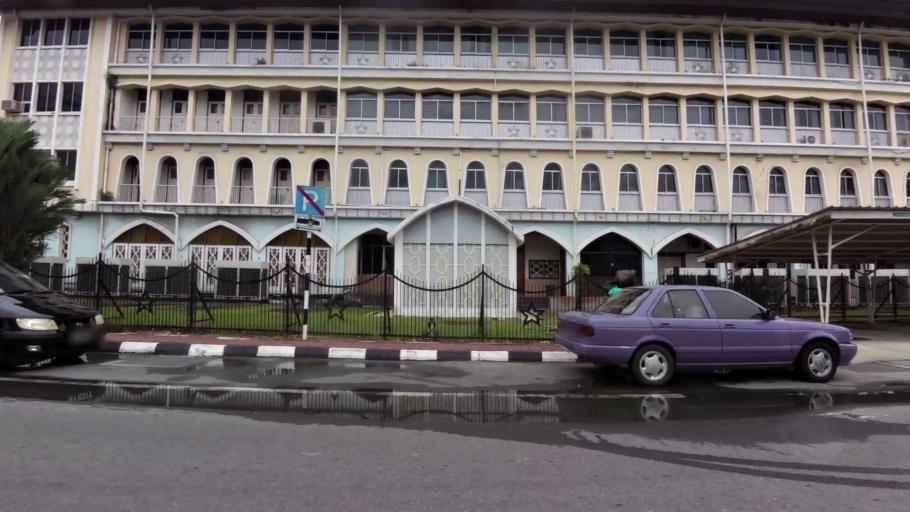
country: BN
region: Brunei and Muara
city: Bandar Seri Begawan
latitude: 4.8908
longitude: 114.9399
